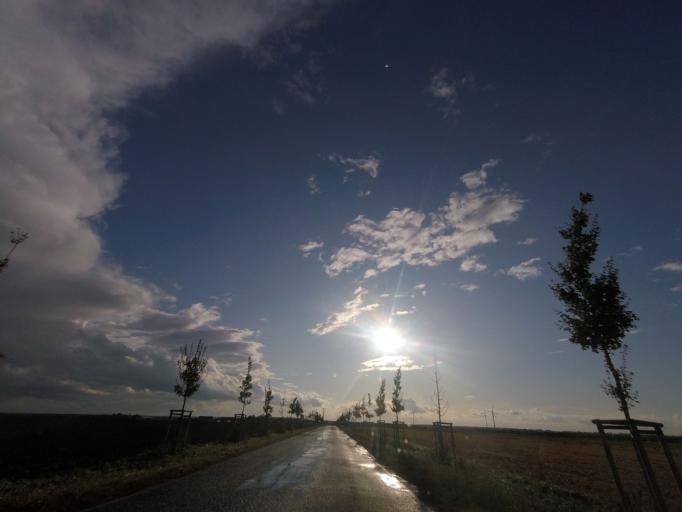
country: DE
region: Saxony-Anhalt
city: Kropstadt
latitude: 52.0066
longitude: 12.7949
